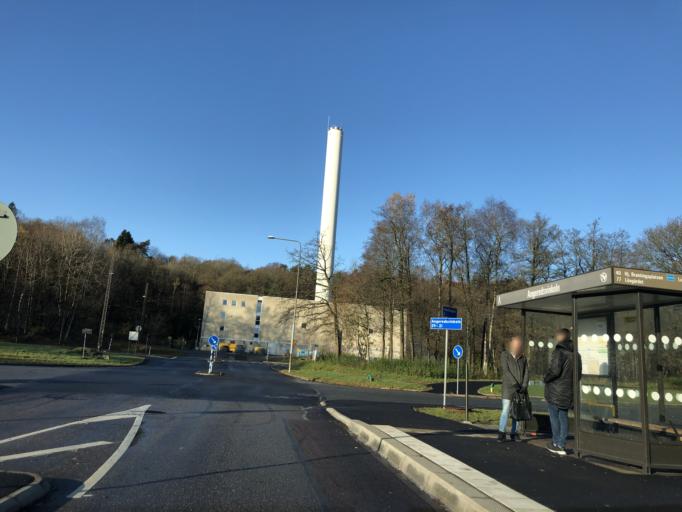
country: SE
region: Vaestra Goetaland
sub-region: Goteborg
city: Gardsten
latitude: 57.8004
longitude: 12.0438
